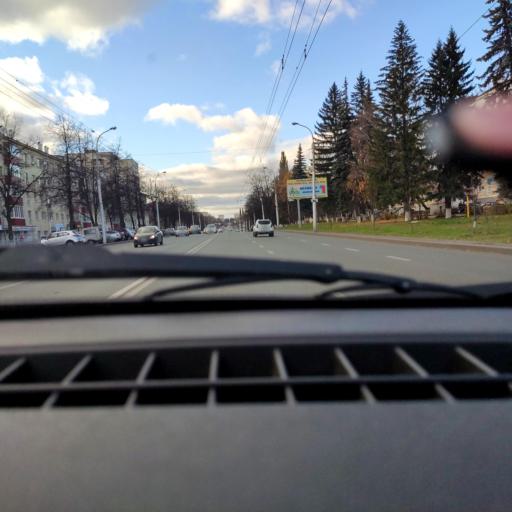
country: RU
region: Bashkortostan
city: Ufa
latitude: 54.8089
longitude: 56.1053
